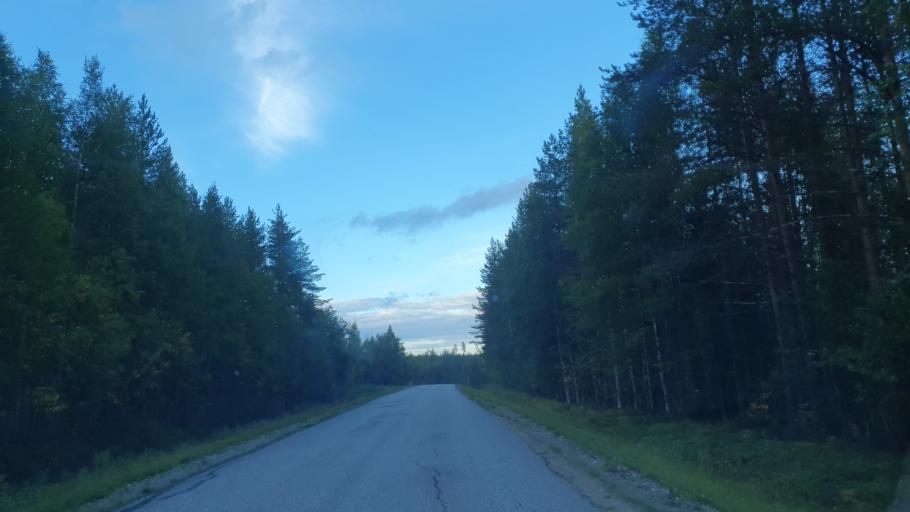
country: FI
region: Kainuu
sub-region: Kehys-Kainuu
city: Kuhmo
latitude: 64.4132
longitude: 29.8862
